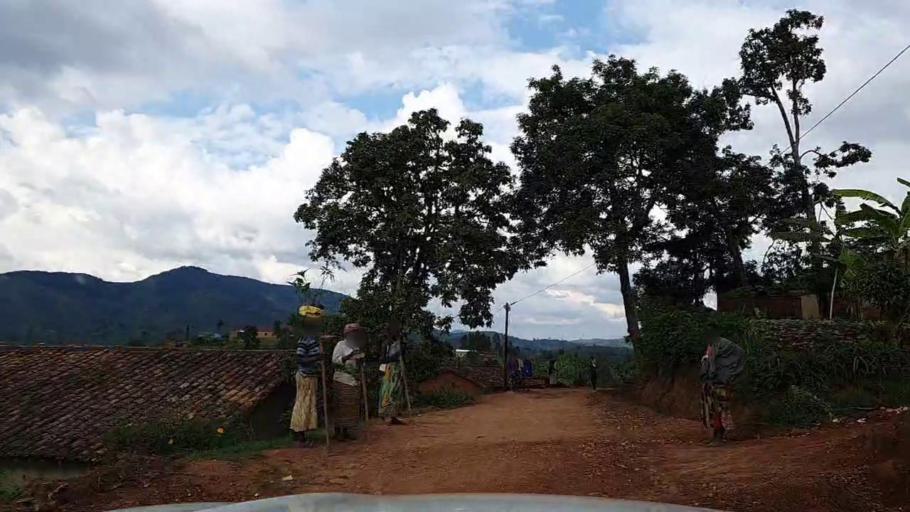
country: RW
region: Southern Province
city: Gikongoro
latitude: -2.4229
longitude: 29.6472
